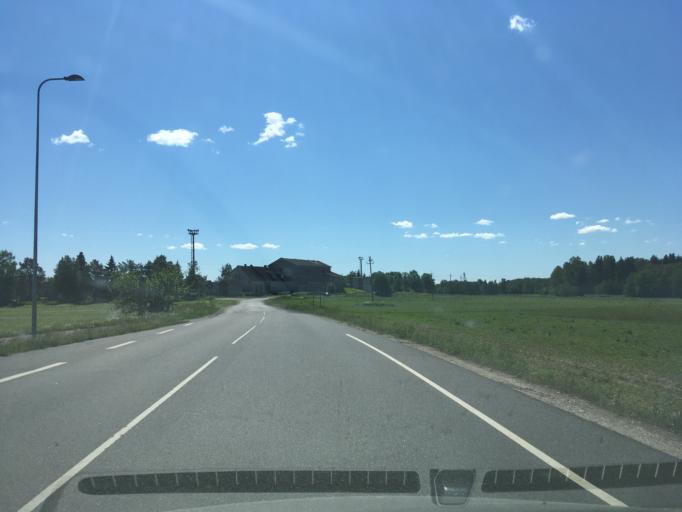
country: EE
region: Harju
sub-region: Raasiku vald
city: Arukula
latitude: 59.1805
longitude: 25.1192
